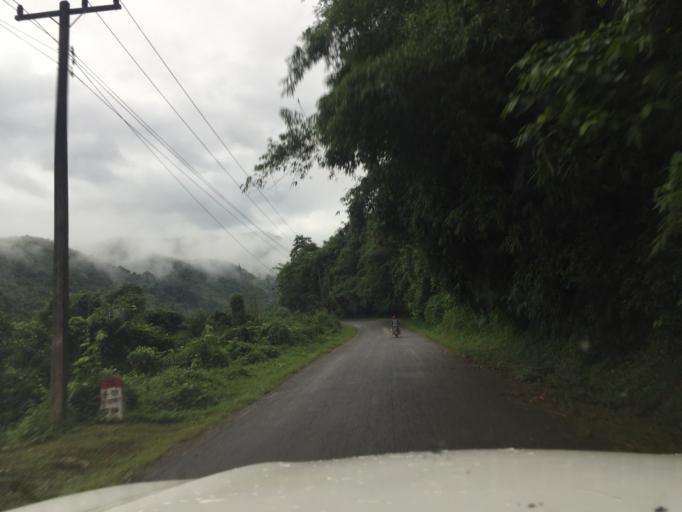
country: LA
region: Oudomxai
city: Muang La
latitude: 20.9036
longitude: 102.1800
